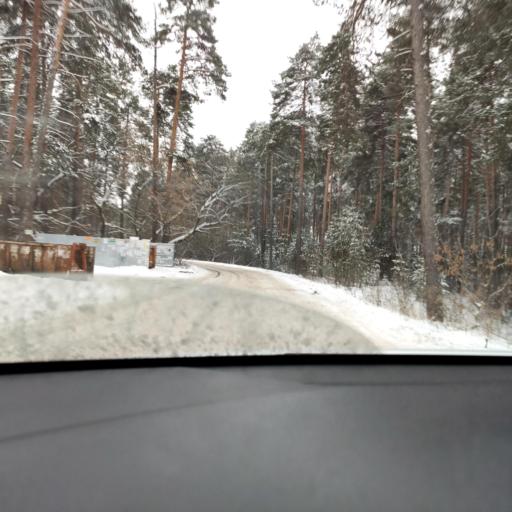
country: RU
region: Tatarstan
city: Osinovo
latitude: 55.8246
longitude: 48.8723
